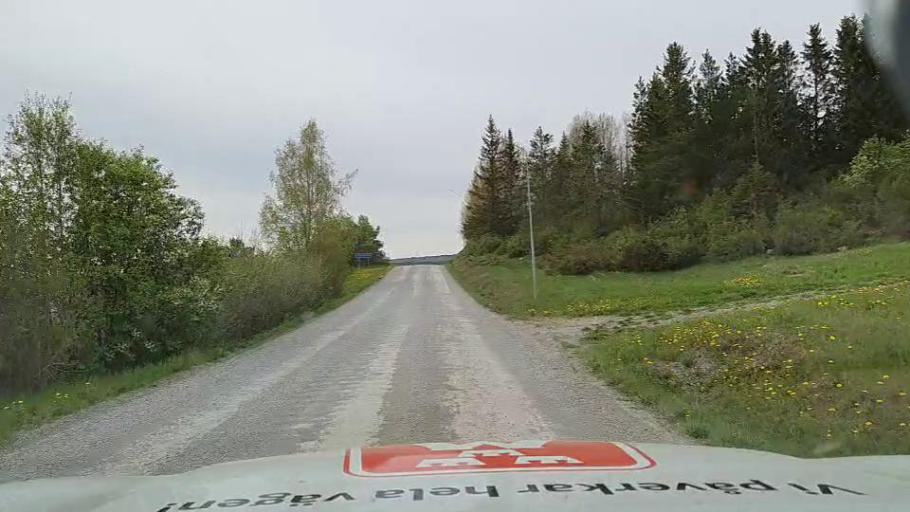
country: SE
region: Jaemtland
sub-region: OEstersunds Kommun
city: Ostersund
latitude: 62.9605
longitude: 14.6405
